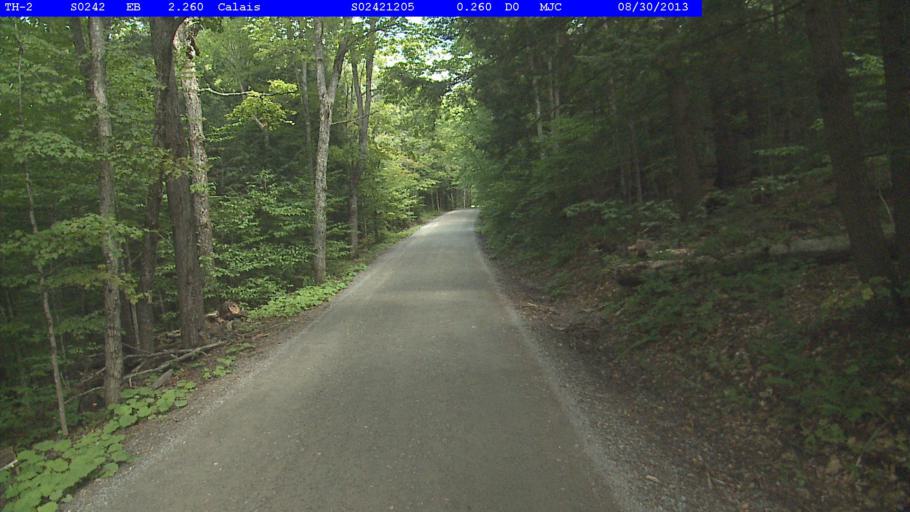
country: US
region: Vermont
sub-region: Washington County
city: Montpelier
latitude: 44.3895
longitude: -72.5153
